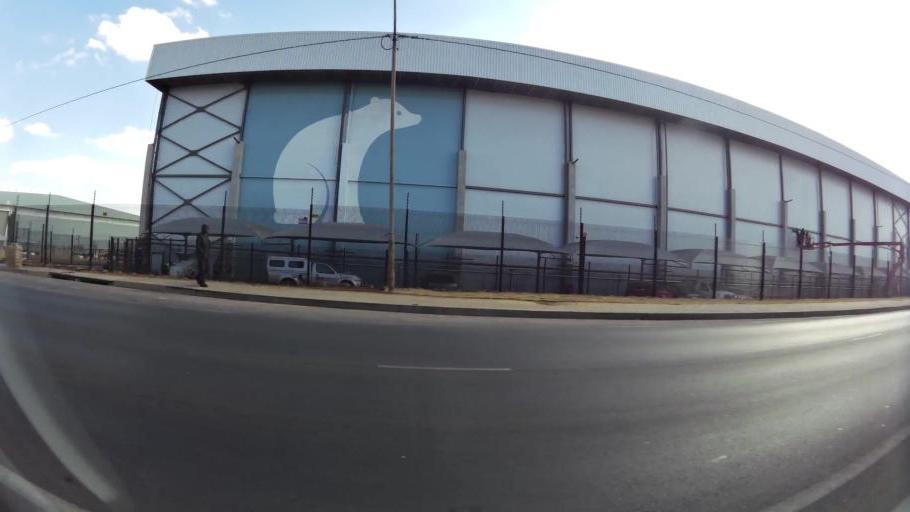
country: ZA
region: Gauteng
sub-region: City of Johannesburg Metropolitan Municipality
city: Johannesburg
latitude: -26.2570
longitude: 27.9730
